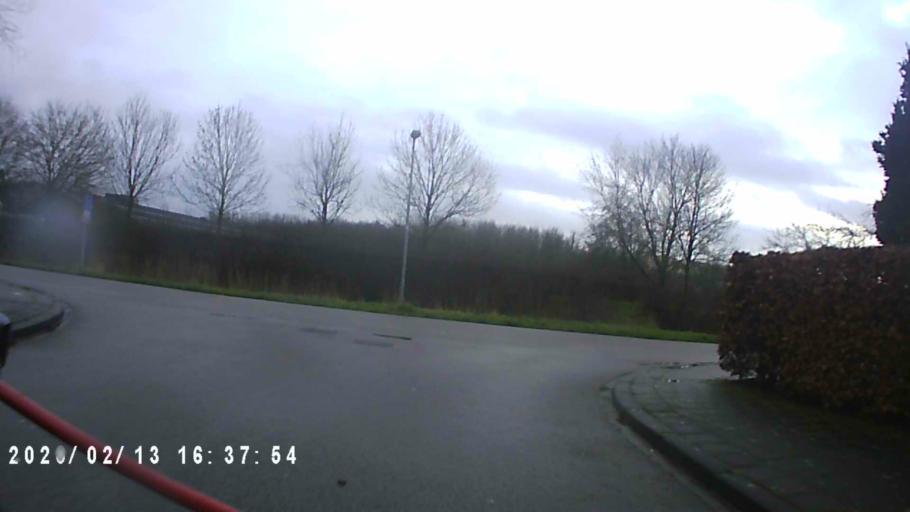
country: NL
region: Groningen
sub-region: Gemeente Groningen
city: Groningen
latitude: 53.2286
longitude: 6.5173
